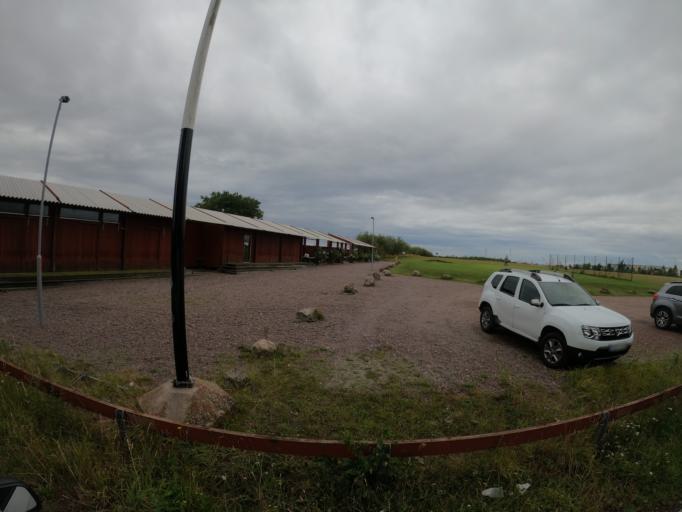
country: SE
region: Skane
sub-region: Lunds Kommun
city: Lund
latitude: 55.7111
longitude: 13.1570
